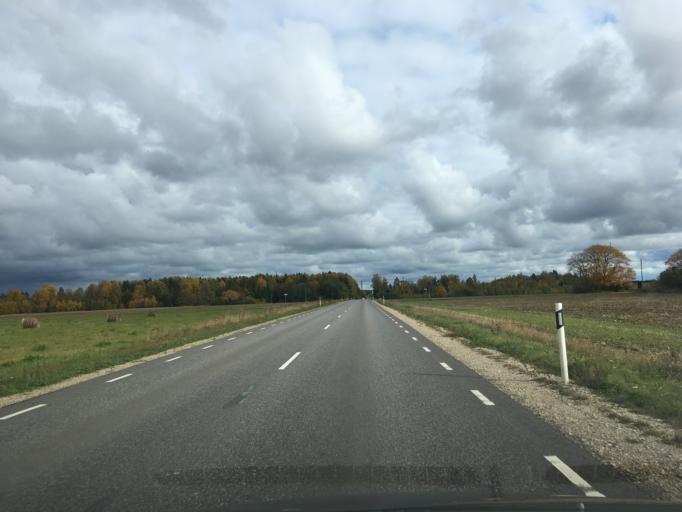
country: EE
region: Harju
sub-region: Anija vald
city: Kehra
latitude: 59.2501
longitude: 25.3130
